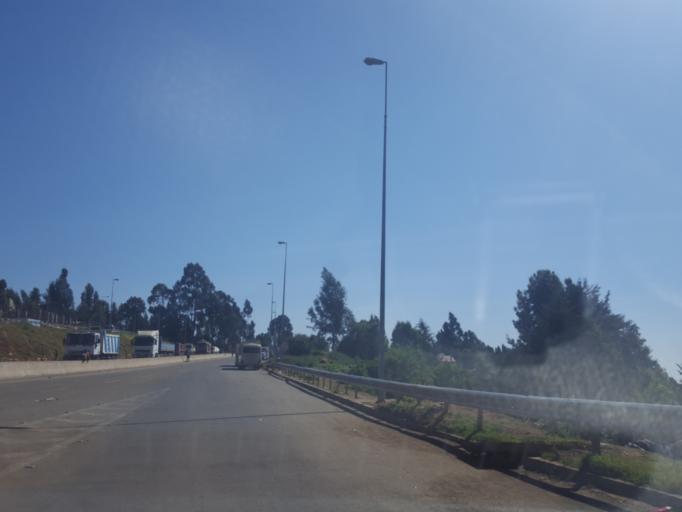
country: ET
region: Adis Abeba
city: Addis Ababa
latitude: 9.0627
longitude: 38.7362
